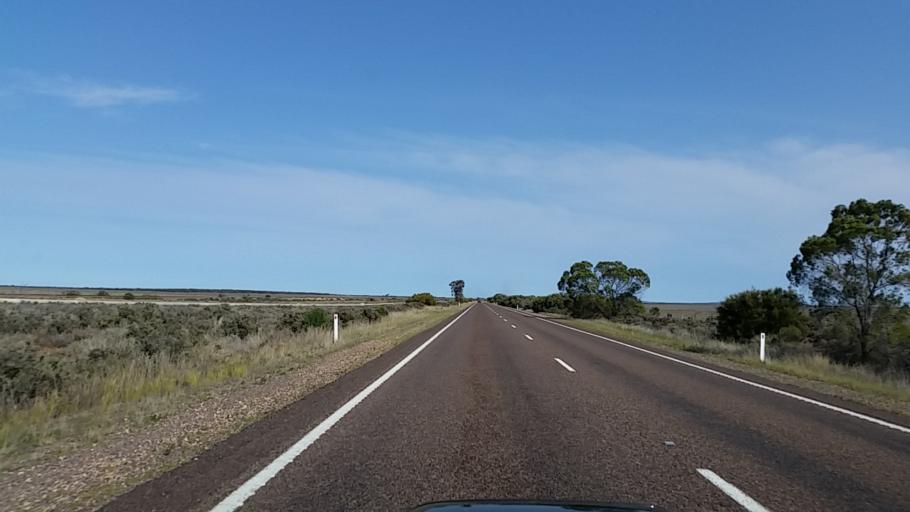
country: AU
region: South Australia
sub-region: Whyalla
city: Whyalla
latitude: -32.8375
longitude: 137.5478
